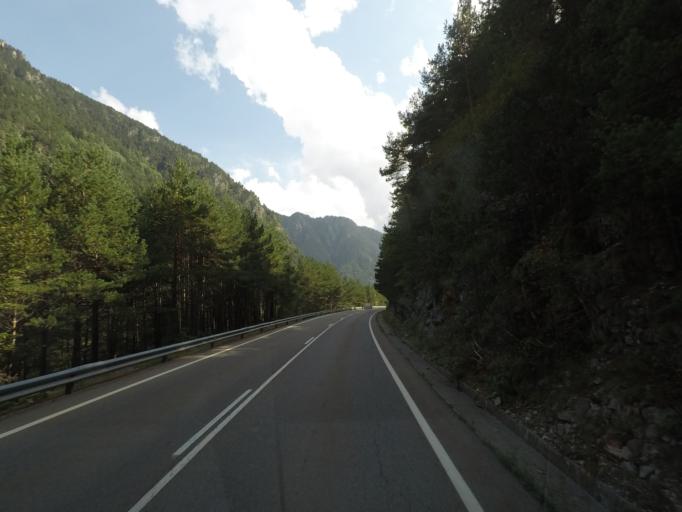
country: ES
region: Aragon
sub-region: Provincia de Huesca
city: Bielsa
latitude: 42.6818
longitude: 0.2130
